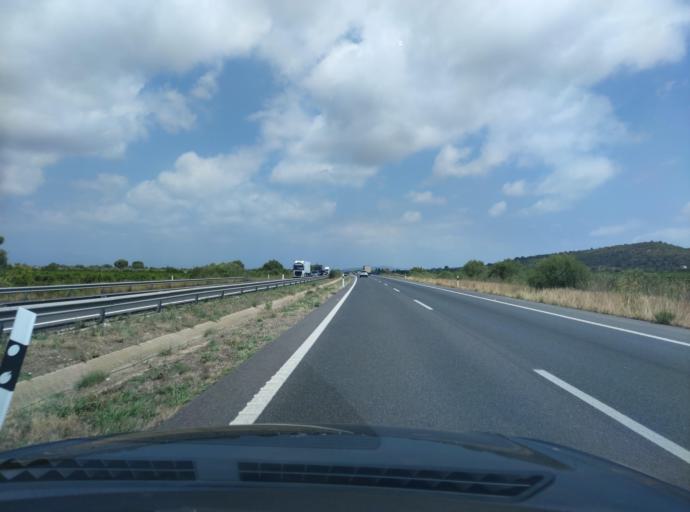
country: ES
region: Valencia
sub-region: Provincia de Castello
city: Vinaros
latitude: 40.4991
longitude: 0.4159
